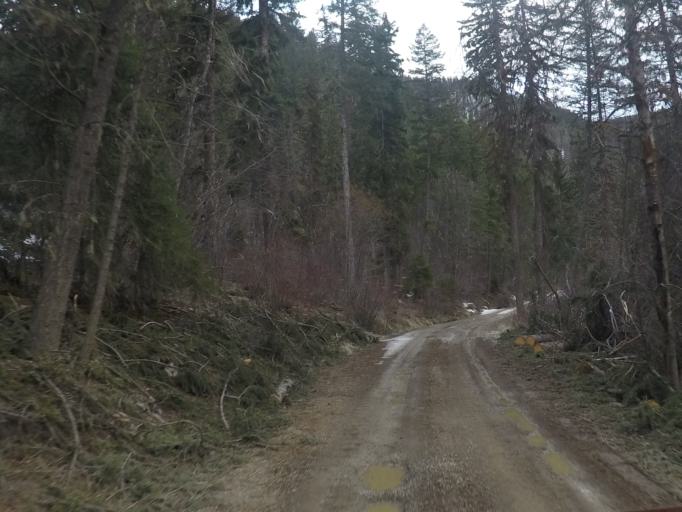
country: US
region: Montana
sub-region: Missoula County
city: Clinton
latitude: 46.5630
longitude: -113.7003
